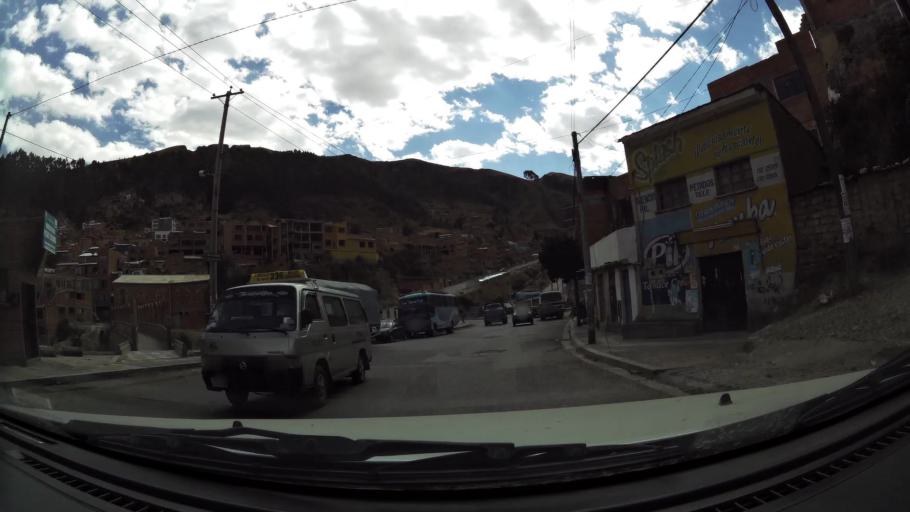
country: BO
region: La Paz
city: La Paz
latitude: -16.4645
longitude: -68.1177
